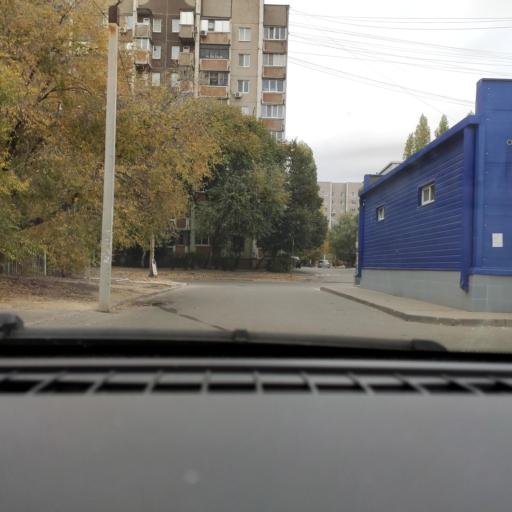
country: RU
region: Voronezj
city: Podgornoye
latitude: 51.7148
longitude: 39.1668
